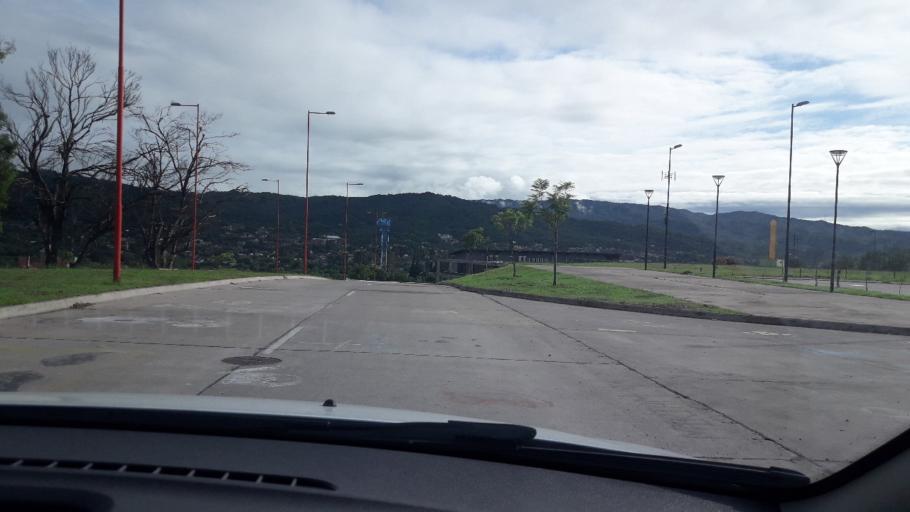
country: AR
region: Jujuy
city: San Salvador de Jujuy
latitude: -24.1811
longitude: -65.3298
